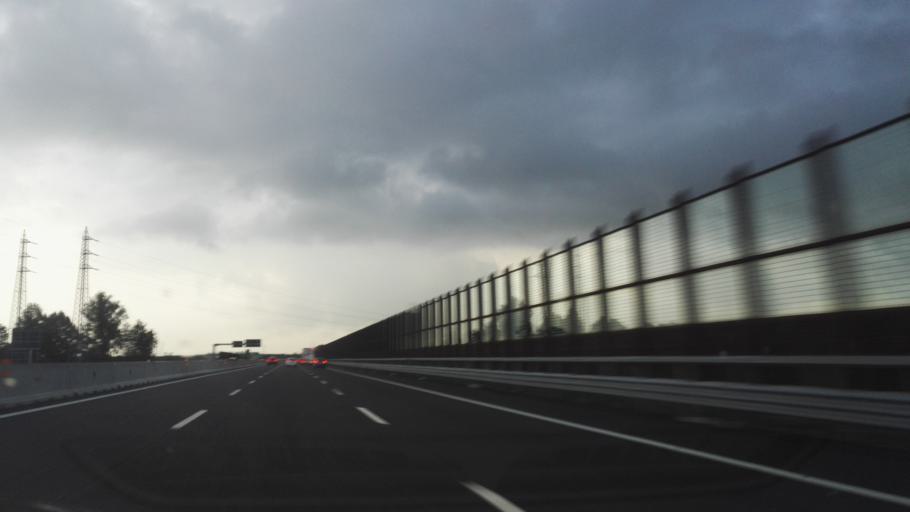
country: IT
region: Lombardy
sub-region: Citta metropolitana di Milano
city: Bellinzago Lombardo
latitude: 45.5259
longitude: 9.4399
